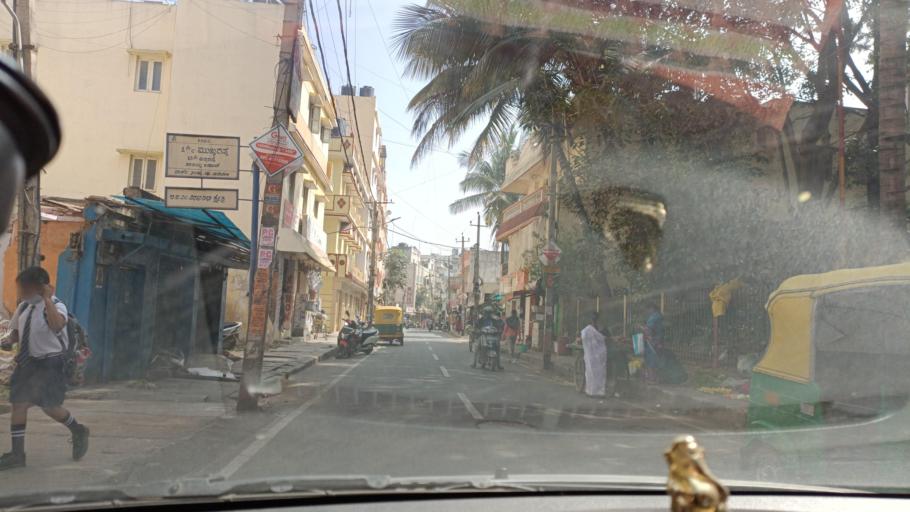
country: IN
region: Karnataka
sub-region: Bangalore Urban
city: Bangalore
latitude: 12.9203
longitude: 77.6166
